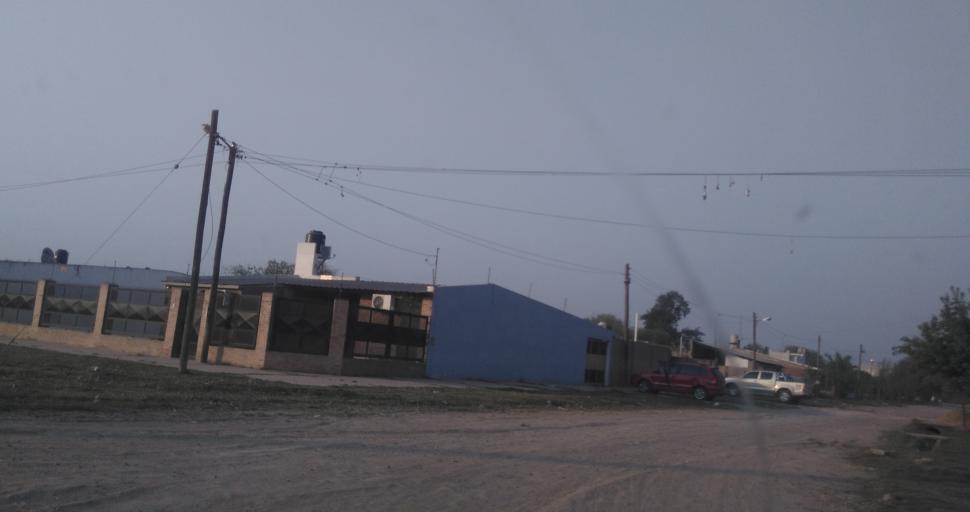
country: AR
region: Chaco
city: Resistencia
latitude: -27.4757
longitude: -59.0035
